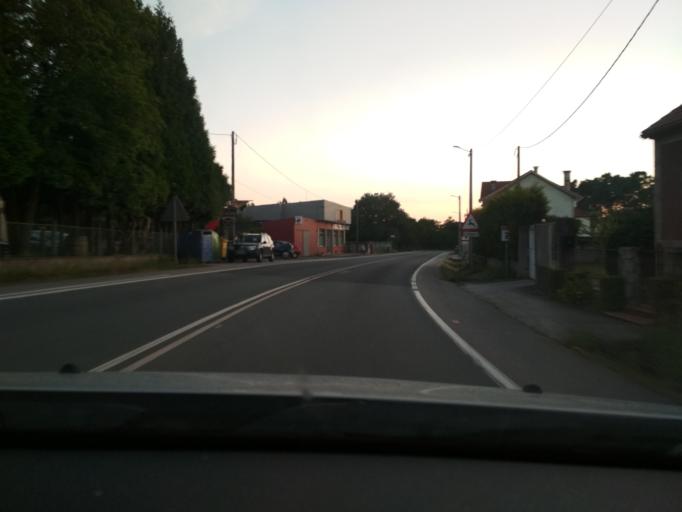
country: ES
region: Galicia
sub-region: Provincia de Pontevedra
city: Catoira
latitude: 42.6705
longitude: -8.7108
